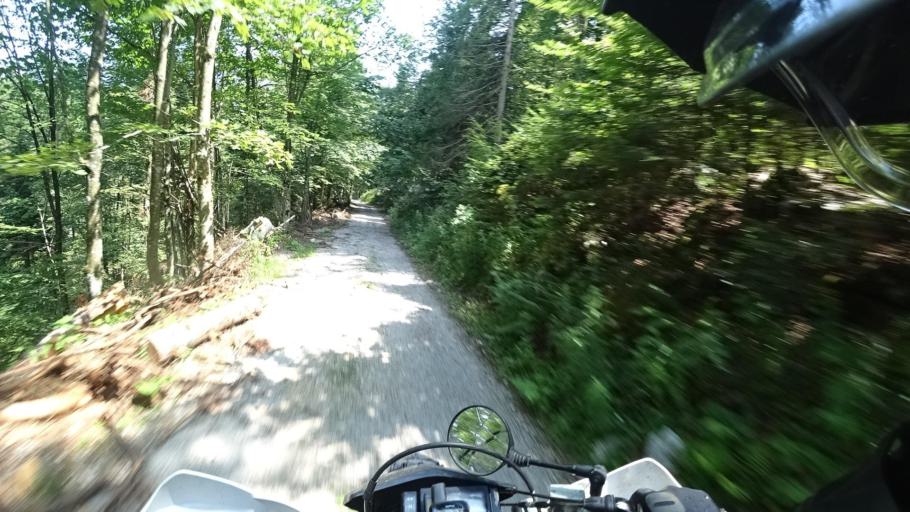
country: HR
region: Primorsko-Goranska
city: Vrbovsko
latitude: 45.3420
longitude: 15.0337
